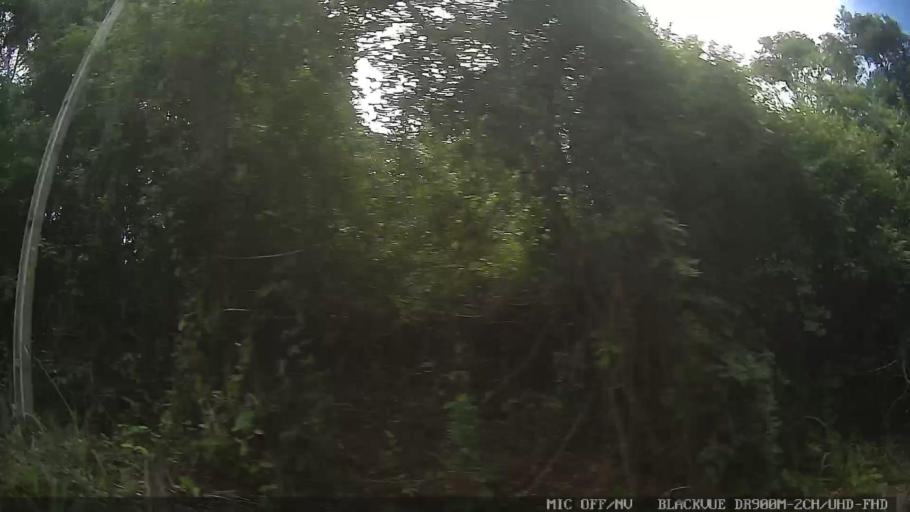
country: BR
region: Sao Paulo
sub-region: Conchas
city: Conchas
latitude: -22.9627
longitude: -47.9818
